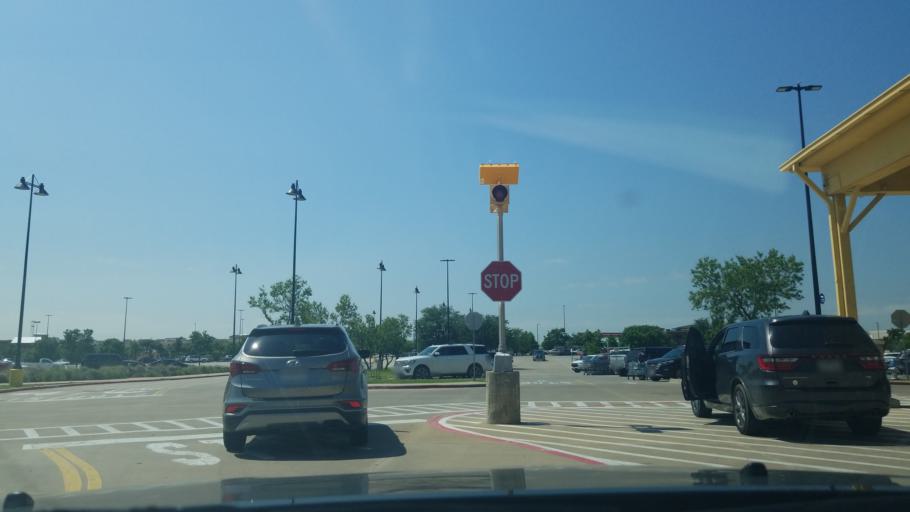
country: US
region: Texas
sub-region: Denton County
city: Denton
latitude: 33.2326
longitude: -97.1693
